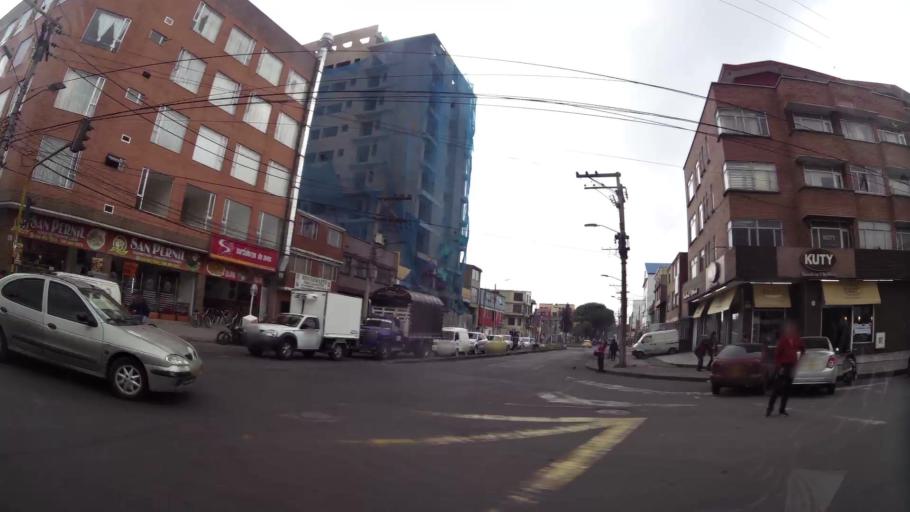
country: CO
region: Bogota D.C.
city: Bogota
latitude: 4.5995
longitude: -74.0949
